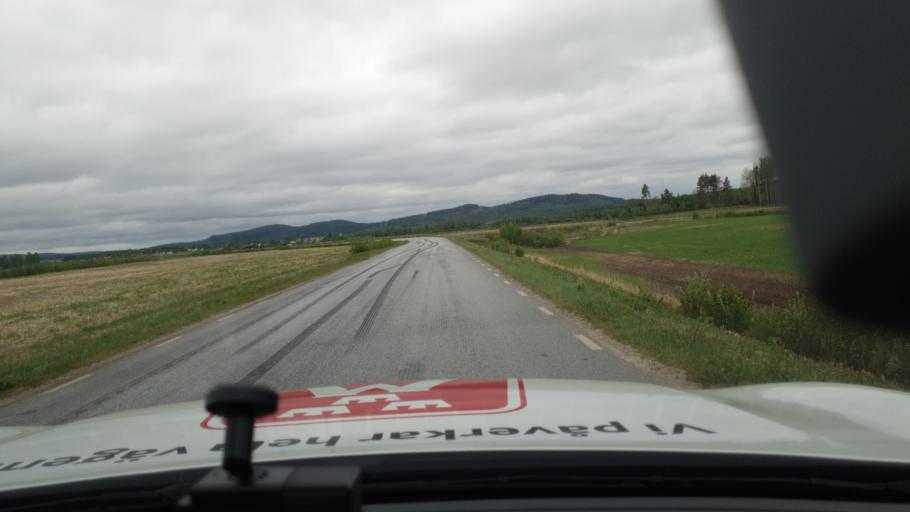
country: SE
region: Vaesterbotten
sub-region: Vannas Kommun
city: Vannasby
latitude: 63.9355
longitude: 19.8349
